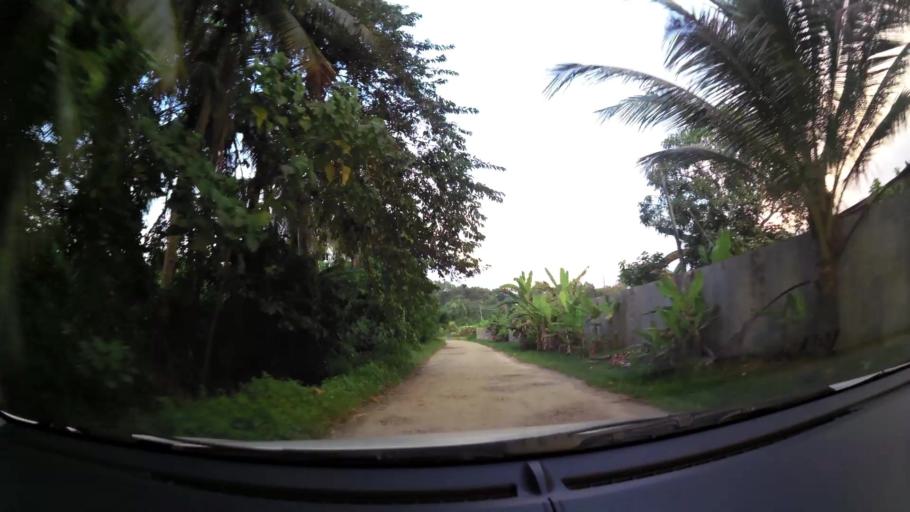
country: BN
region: Brunei and Muara
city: Bandar Seri Begawan
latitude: 4.9995
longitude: 114.9978
